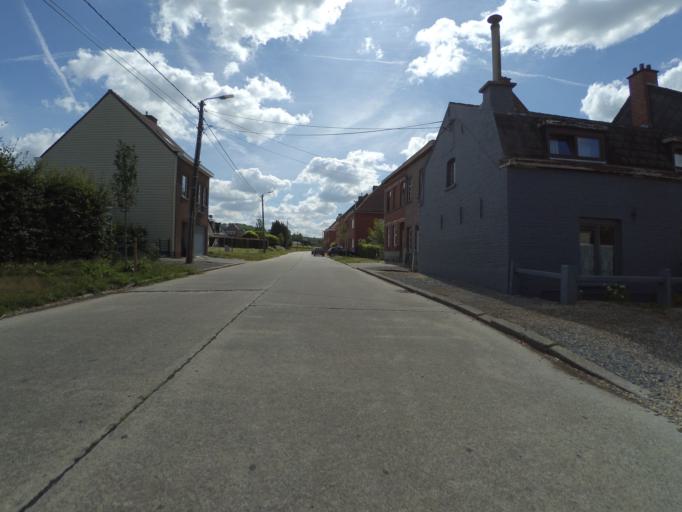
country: BE
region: Flanders
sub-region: Provincie Oost-Vlaanderen
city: Ronse
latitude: 50.7346
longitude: 3.6160
